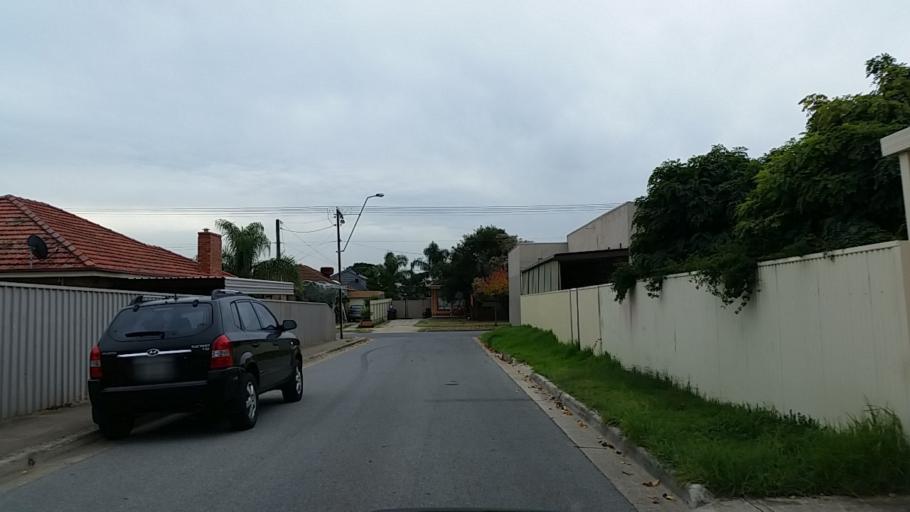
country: AU
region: South Australia
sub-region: Charles Sturt
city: Royal Park
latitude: -34.8774
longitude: 138.5086
